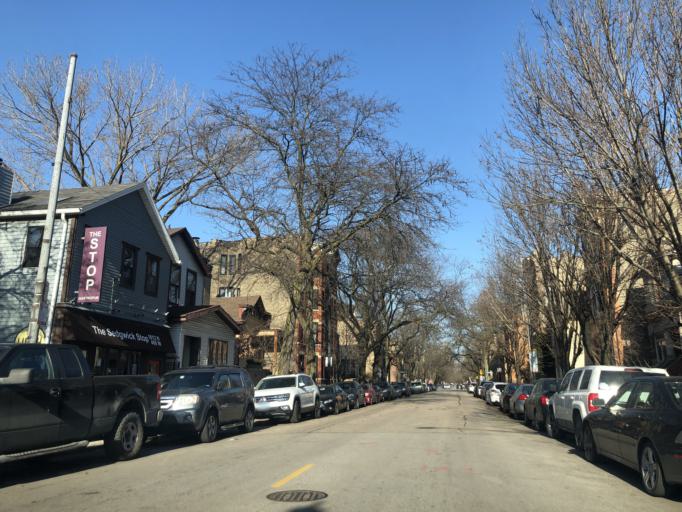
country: US
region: Illinois
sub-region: Cook County
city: Chicago
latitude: 41.9112
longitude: -87.6385
